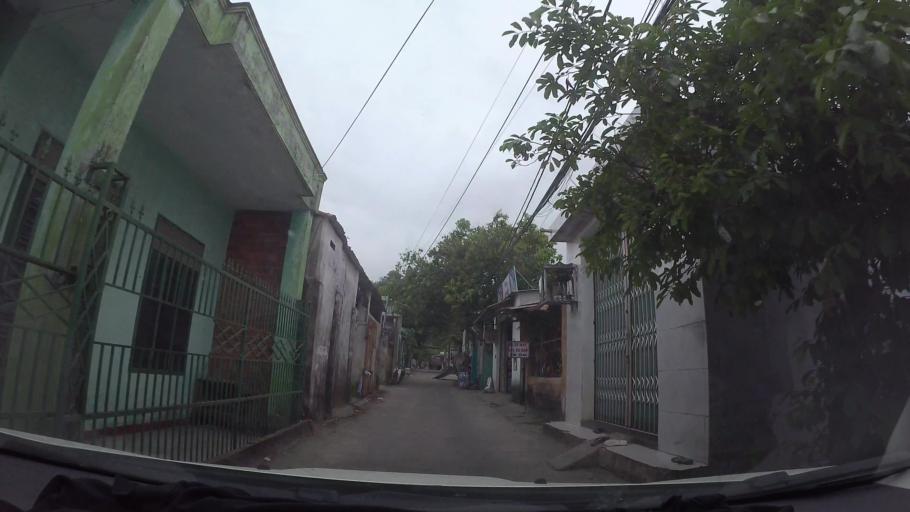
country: VN
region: Da Nang
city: Lien Chieu
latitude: 16.0722
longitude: 108.1380
